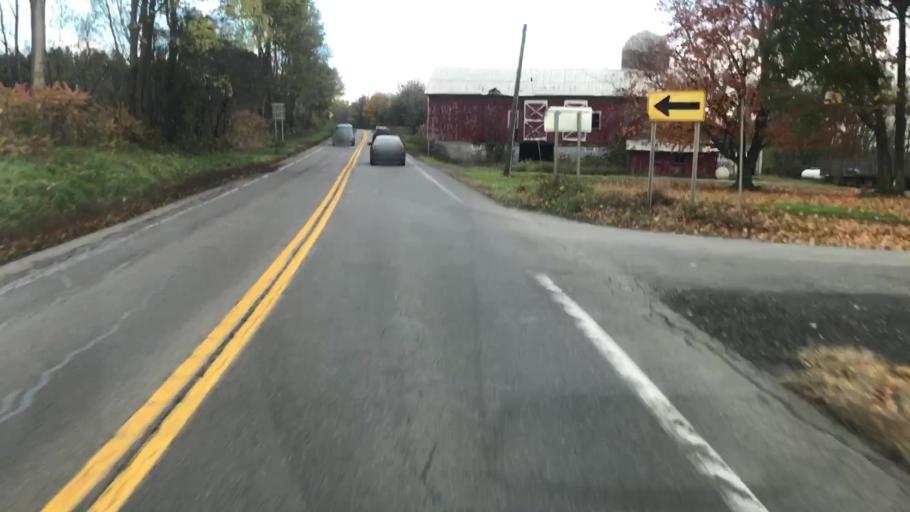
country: US
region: New York
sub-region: Onondaga County
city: Elbridge
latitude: 43.0167
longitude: -76.4012
